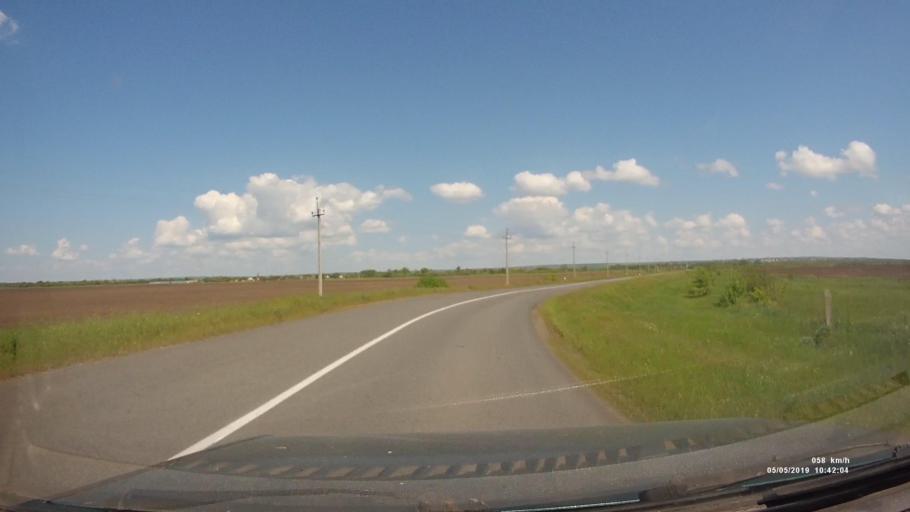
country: RU
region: Rostov
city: Ust'-Donetskiy
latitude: 47.5958
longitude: 40.8371
